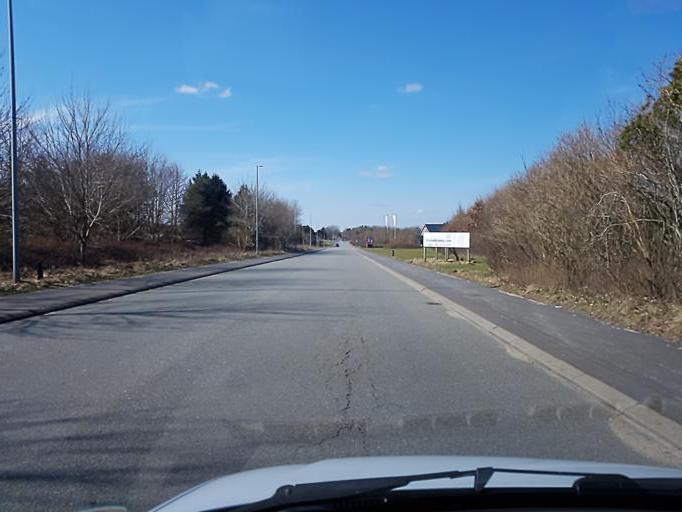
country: DK
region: South Denmark
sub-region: Varde Kommune
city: Varde
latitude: 55.6078
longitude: 8.5046
